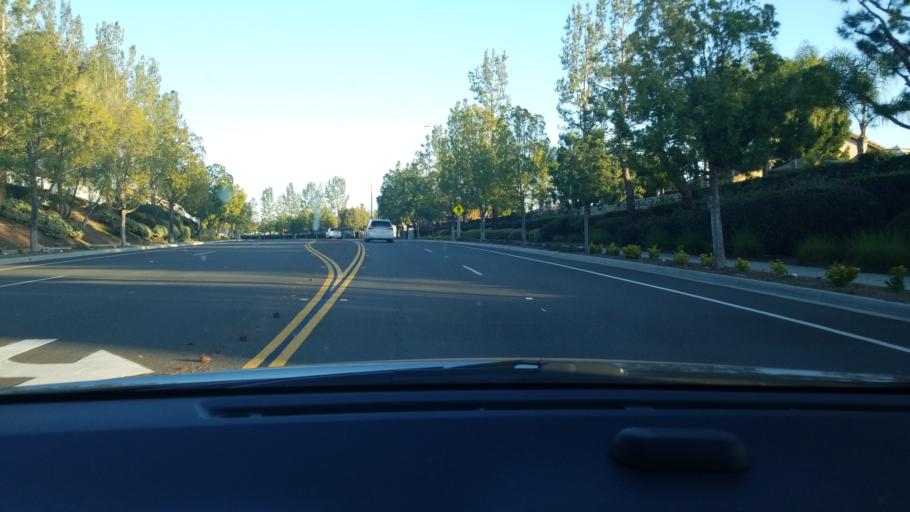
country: US
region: California
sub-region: Riverside County
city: Murrieta Hot Springs
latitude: 33.5451
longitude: -117.1384
